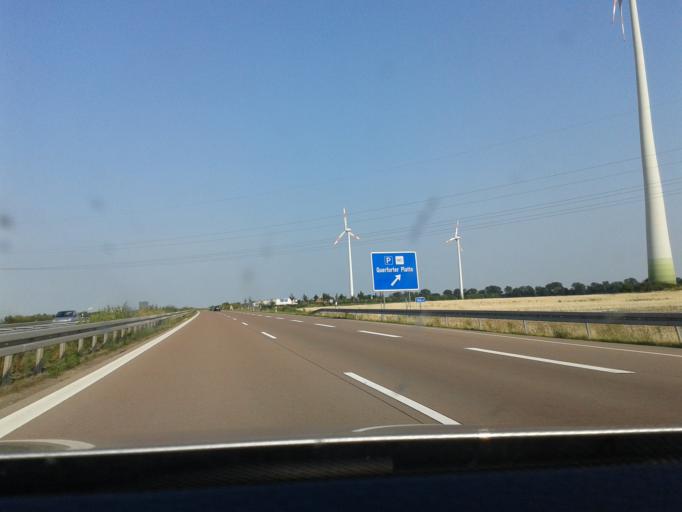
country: DE
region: Saxony-Anhalt
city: Stedten
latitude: 51.4006
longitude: 11.7206
